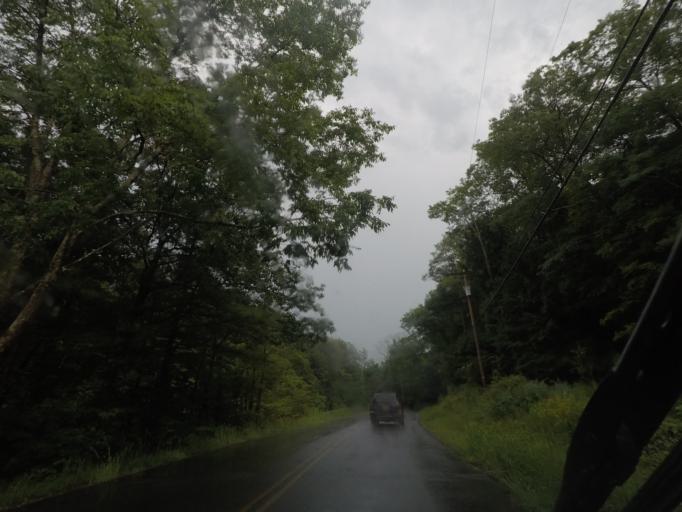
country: US
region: New York
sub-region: Rensselaer County
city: Poestenkill
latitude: 42.6777
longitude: -73.5384
